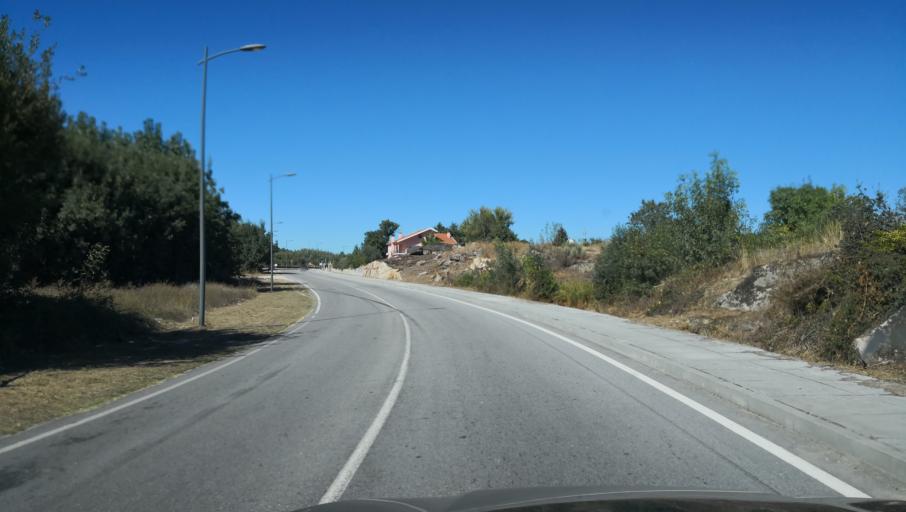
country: PT
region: Vila Real
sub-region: Valpacos
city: Valpacos
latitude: 41.5864
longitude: -7.3062
